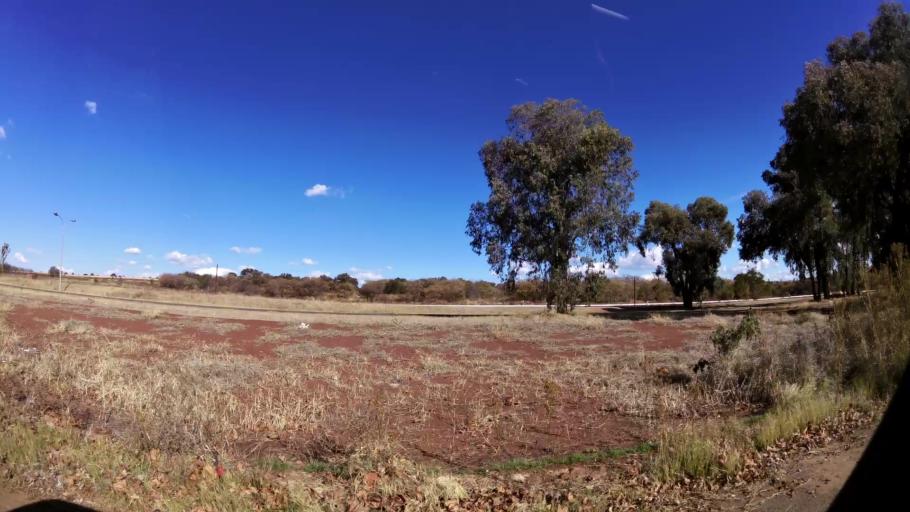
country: ZA
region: Gauteng
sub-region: West Rand District Municipality
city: Carletonville
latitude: -26.3754
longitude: 27.3999
